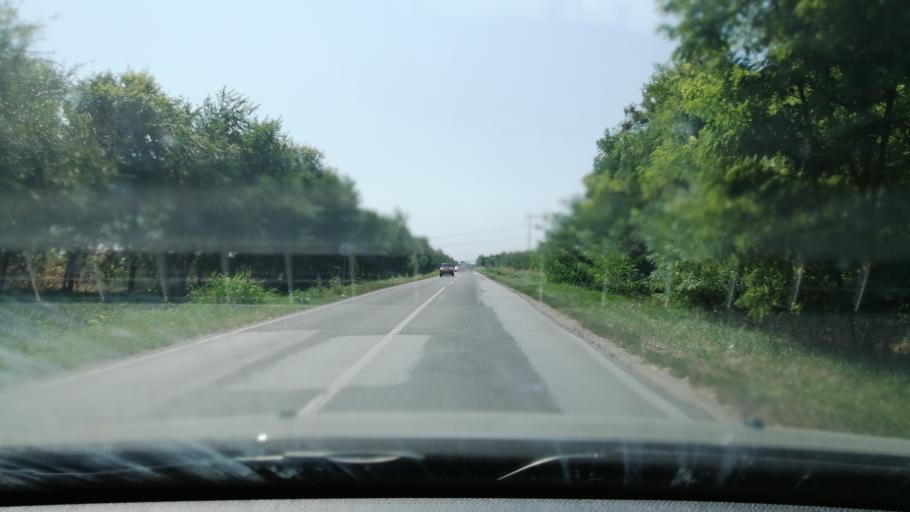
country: RS
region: Autonomna Pokrajina Vojvodina
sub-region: Juznobanatski Okrug
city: Pancevo
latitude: 44.7900
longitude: 20.7236
